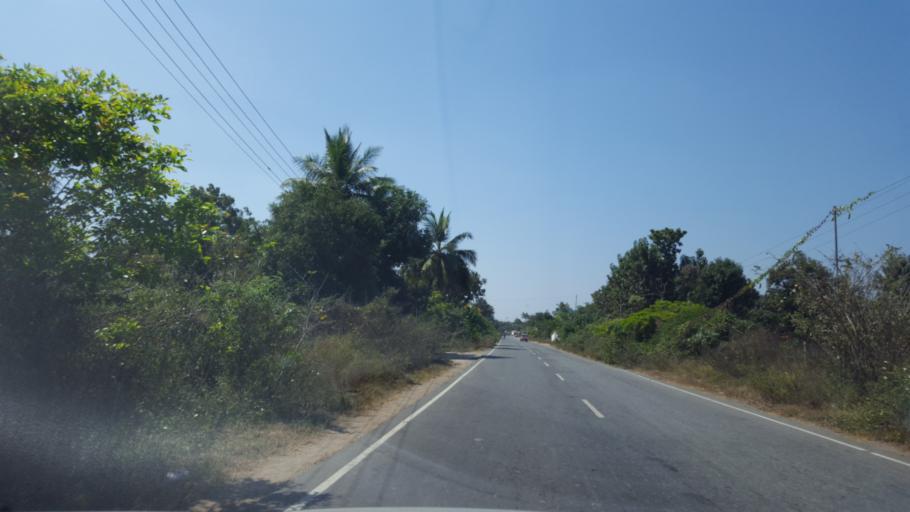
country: IN
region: Tamil Nadu
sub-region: Kancheepuram
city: Chengalpattu
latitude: 12.7618
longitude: 79.9127
